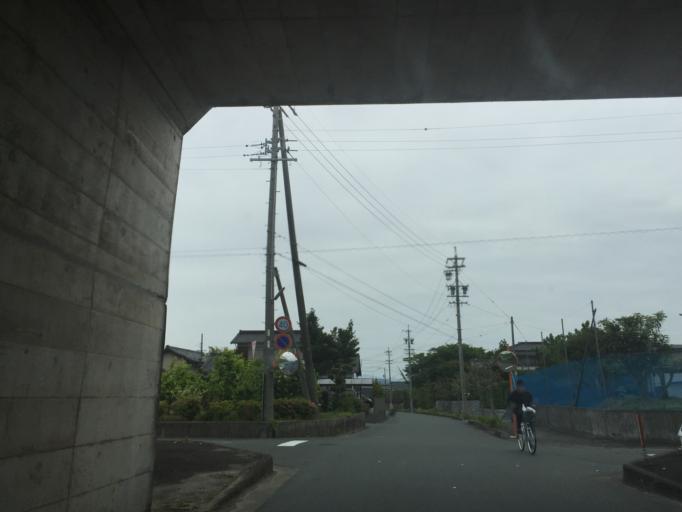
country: JP
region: Shizuoka
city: Kakegawa
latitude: 34.7647
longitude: 137.9939
